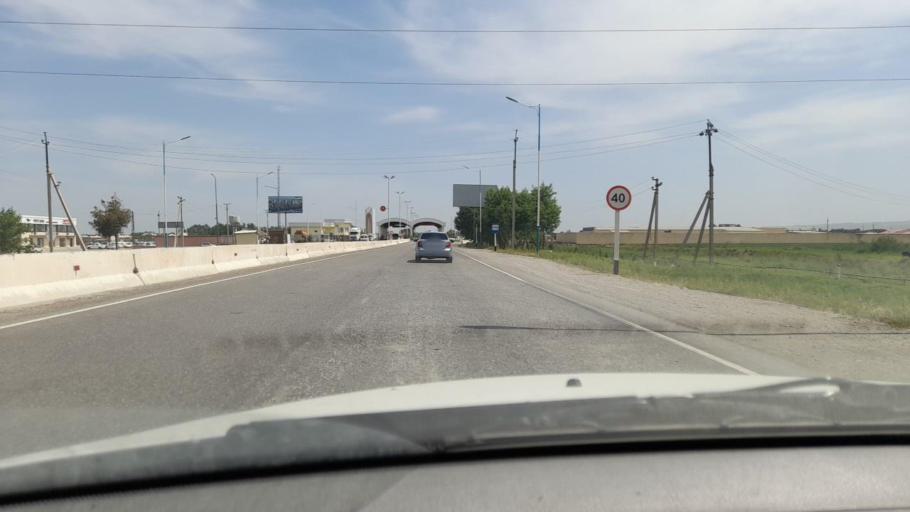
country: UZ
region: Navoiy
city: Karmana Shahri
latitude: 40.1197
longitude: 65.4862
